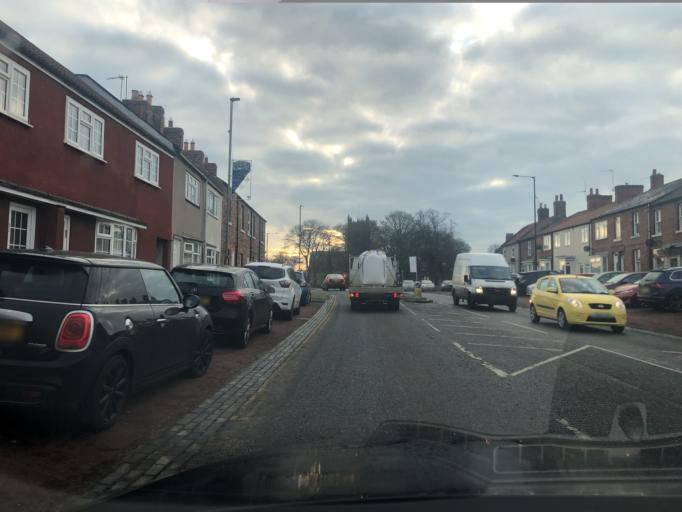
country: GB
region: England
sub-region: North Yorkshire
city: Northallerton
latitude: 54.3440
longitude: -1.4380
